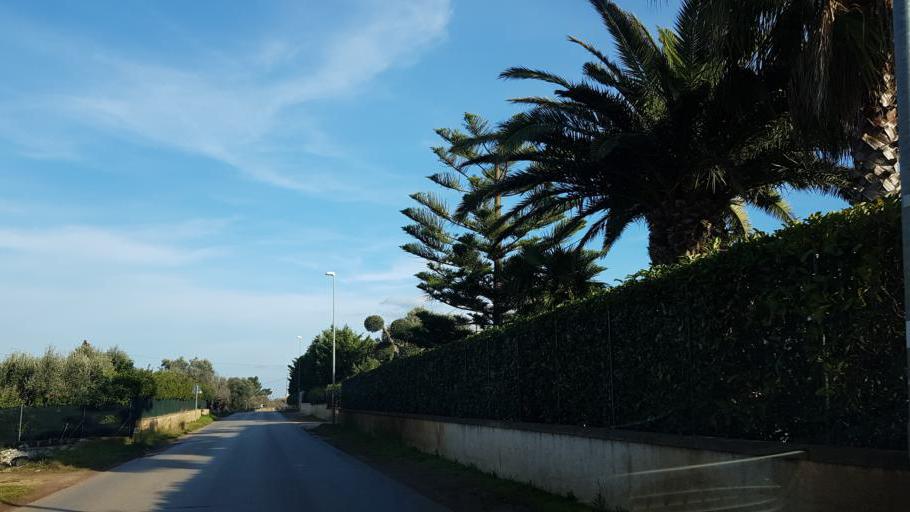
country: IT
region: Apulia
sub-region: Provincia di Brindisi
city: Carovigno
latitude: 40.7010
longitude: 17.6746
